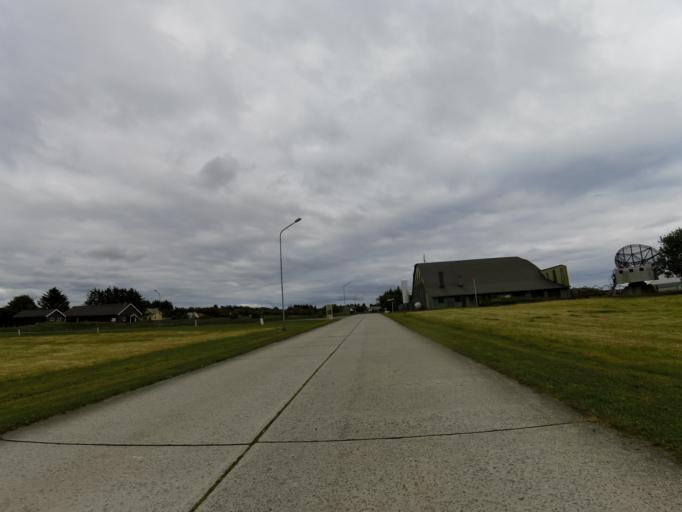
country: NO
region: Vest-Agder
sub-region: Farsund
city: Vestbygd
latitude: 58.1142
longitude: 6.6152
